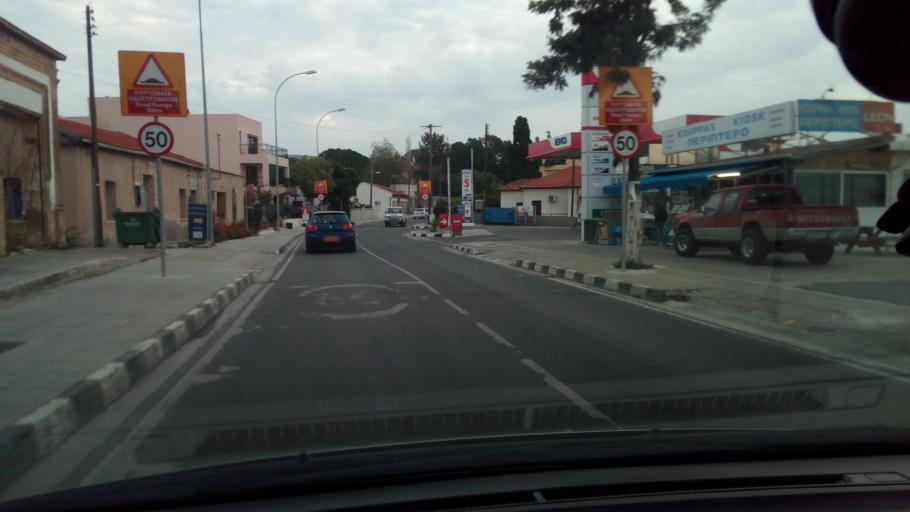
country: CY
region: Pafos
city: Polis
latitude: 35.0326
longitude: 32.4272
